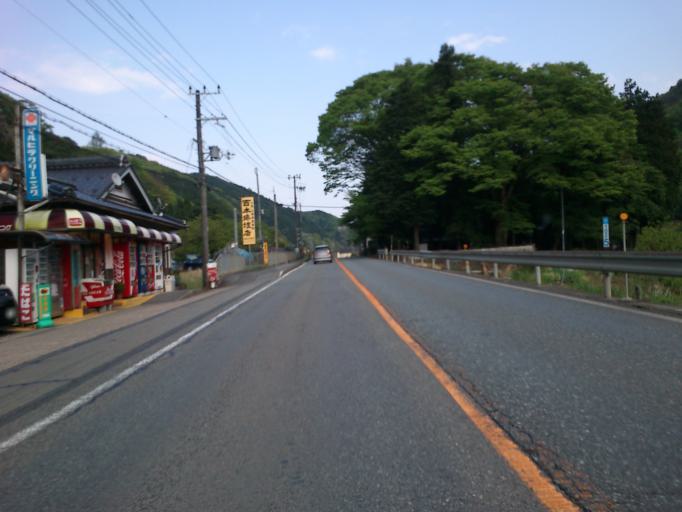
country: JP
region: Kyoto
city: Fukuchiyama
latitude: 35.3242
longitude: 134.9700
